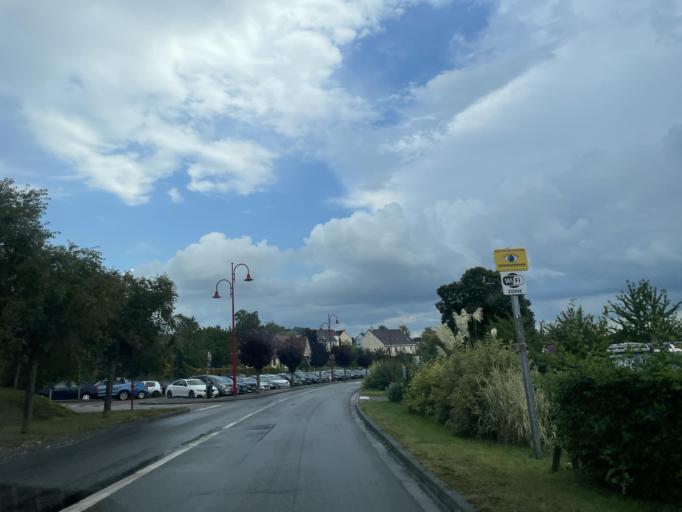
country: FR
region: Haute-Normandie
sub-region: Departement de la Seine-Maritime
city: Neufchatel-en-Bray
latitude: 49.7427
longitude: 1.4360
